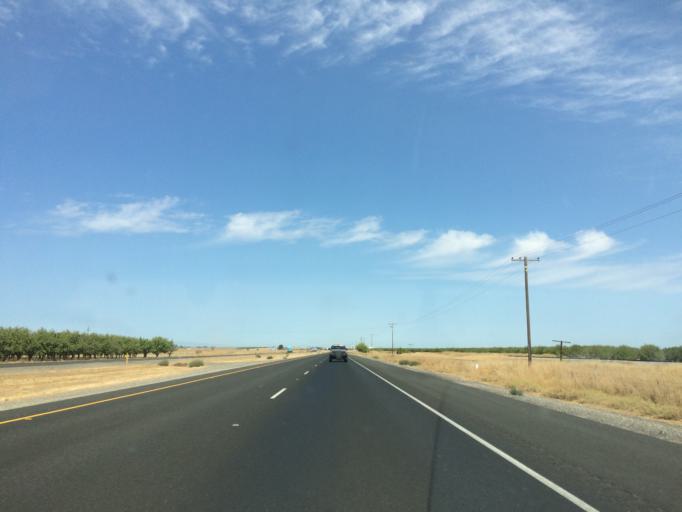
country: US
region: California
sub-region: Yolo County
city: Dunnigan
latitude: 38.9385
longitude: -122.0053
